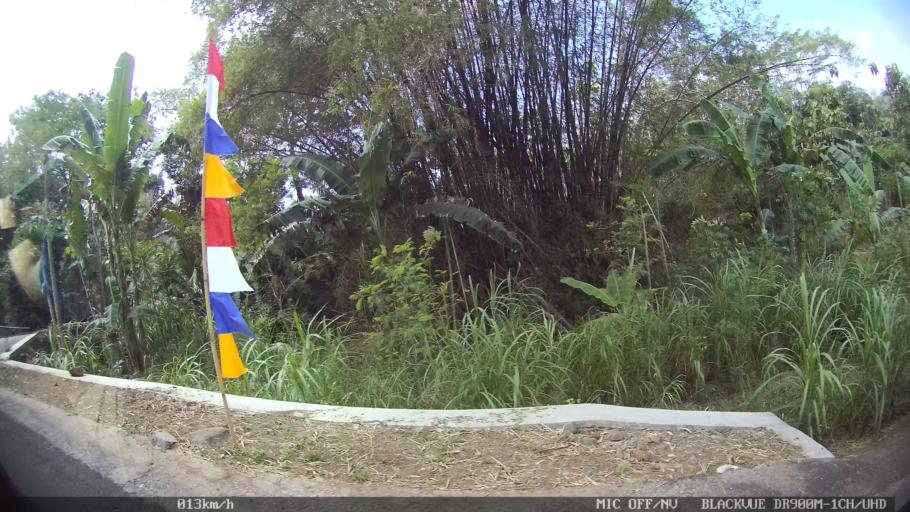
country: ID
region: Central Java
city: Candi Prambanan
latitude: -7.8202
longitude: 110.5241
